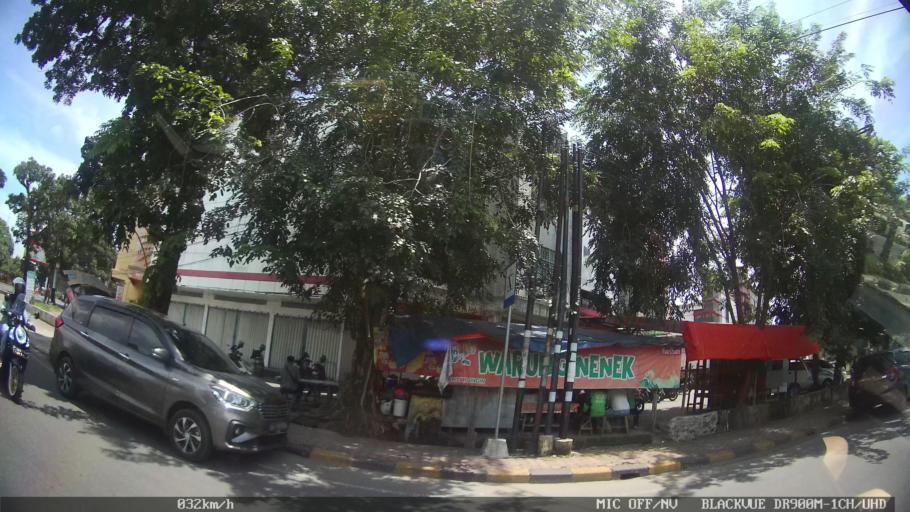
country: ID
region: North Sumatra
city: Binjai
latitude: 3.6088
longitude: 98.4952
